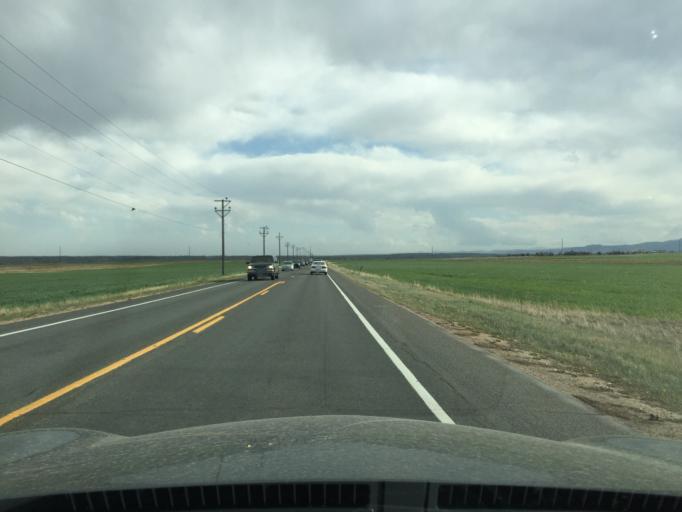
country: US
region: Colorado
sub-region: Boulder County
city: Niwot
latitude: 40.0844
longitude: -105.1315
